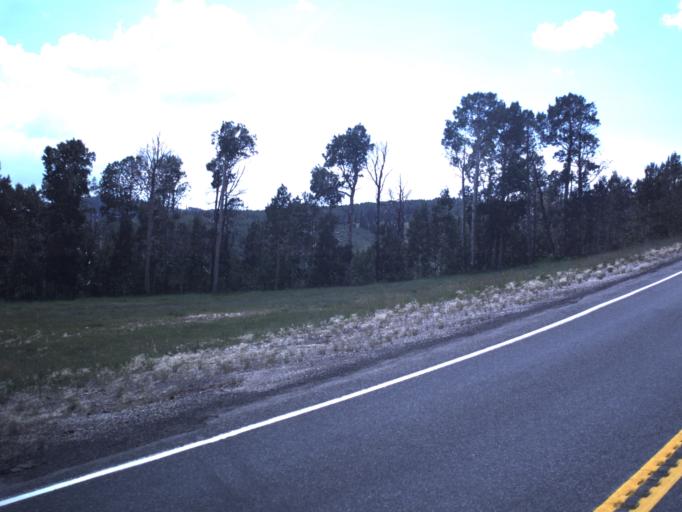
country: US
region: Utah
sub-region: Sanpete County
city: Fairview
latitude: 39.6832
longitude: -111.2133
